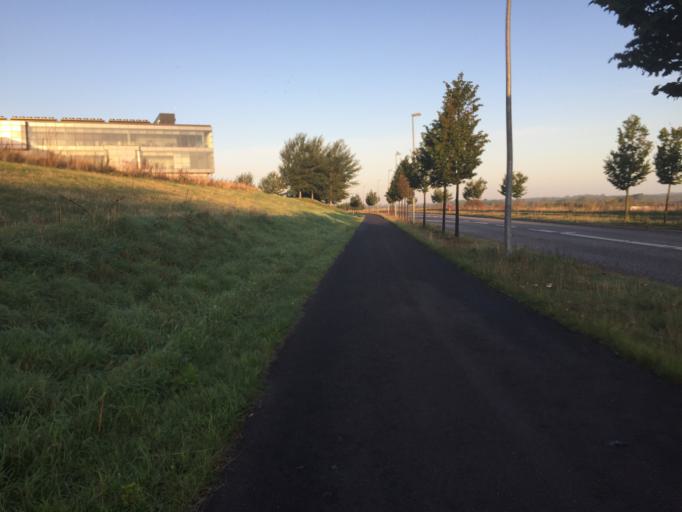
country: DK
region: Capital Region
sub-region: Egedal Kommune
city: Smorumnedre
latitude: 55.7492
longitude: 12.2969
